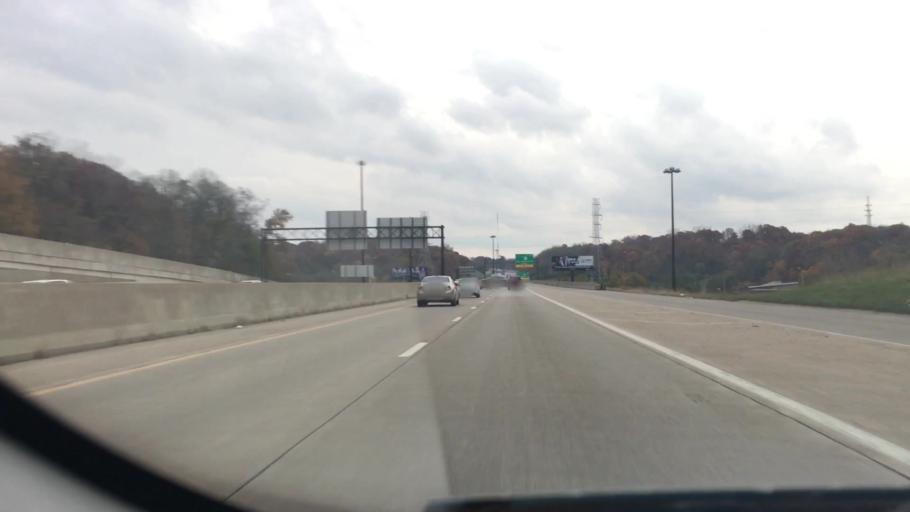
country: US
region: Illinois
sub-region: Tazewell County
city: East Peoria
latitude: 40.6683
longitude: -89.5723
